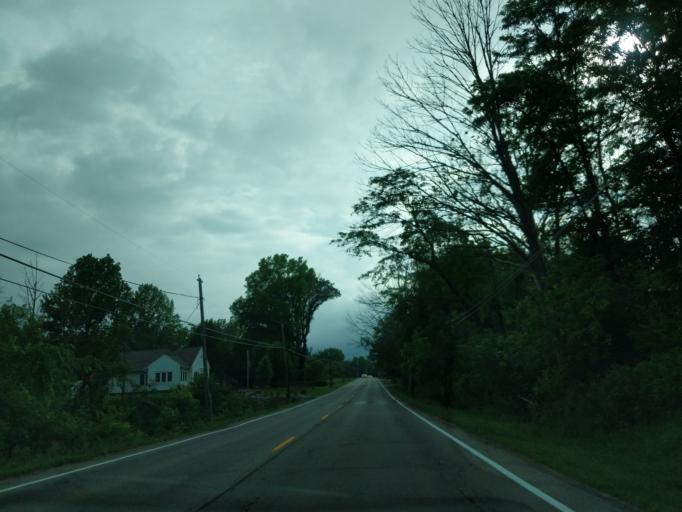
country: US
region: Indiana
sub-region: Delaware County
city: Yorktown
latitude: 40.1686
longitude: -85.5076
